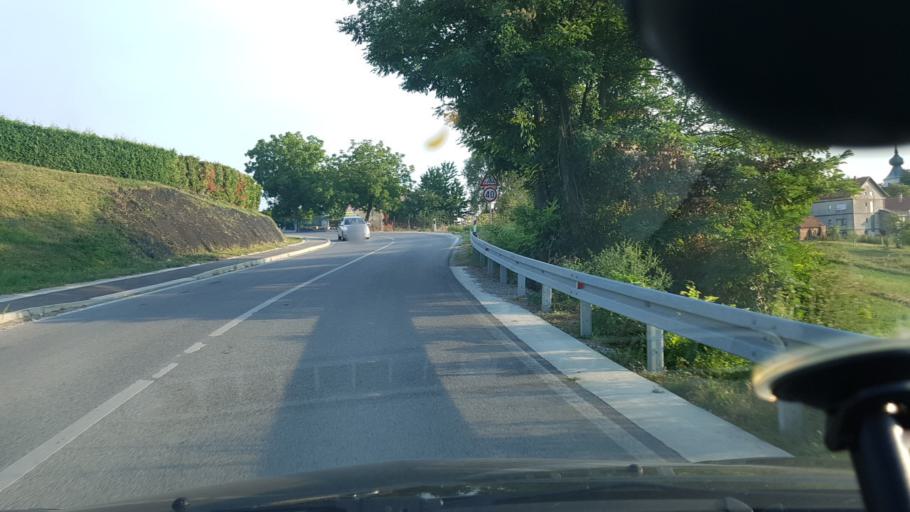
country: HR
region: Krapinsko-Zagorska
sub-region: Grad Krapina
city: Krapina
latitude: 46.1691
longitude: 15.8427
